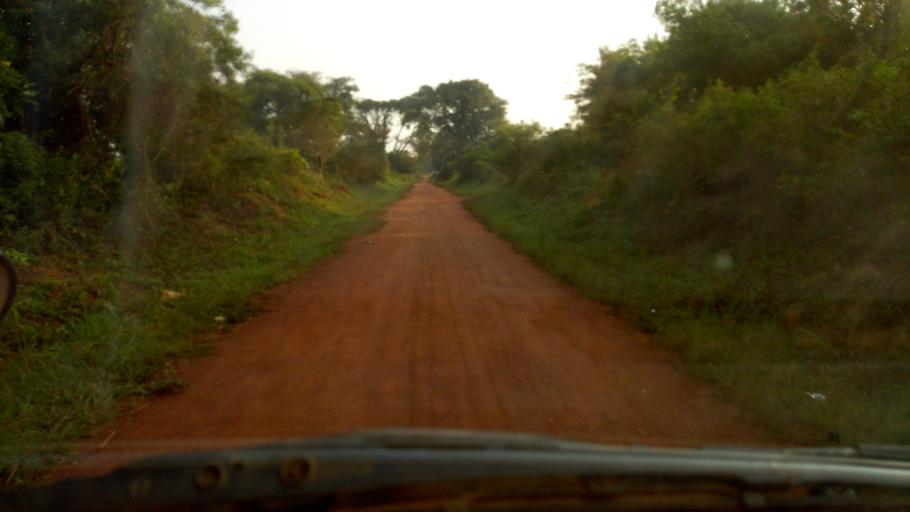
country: UG
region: Western Region
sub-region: Masindi District
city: Masindi
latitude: 1.7717
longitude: 31.8396
